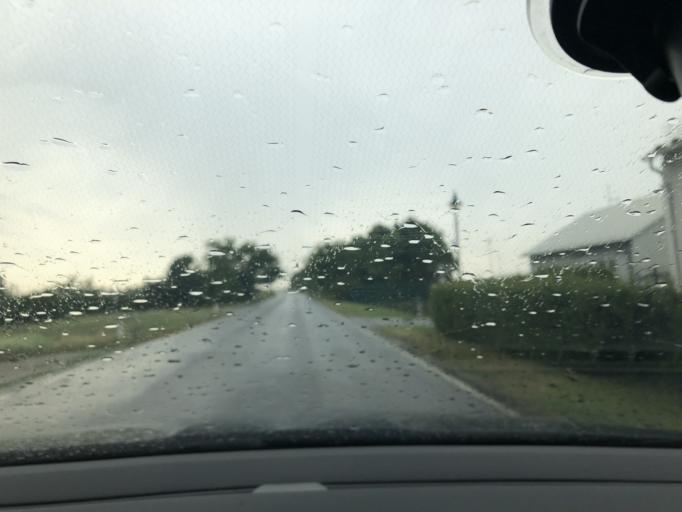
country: AT
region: Lower Austria
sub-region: Politischer Bezirk Ganserndorf
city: Ganserndorf
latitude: 48.3679
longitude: 16.6891
